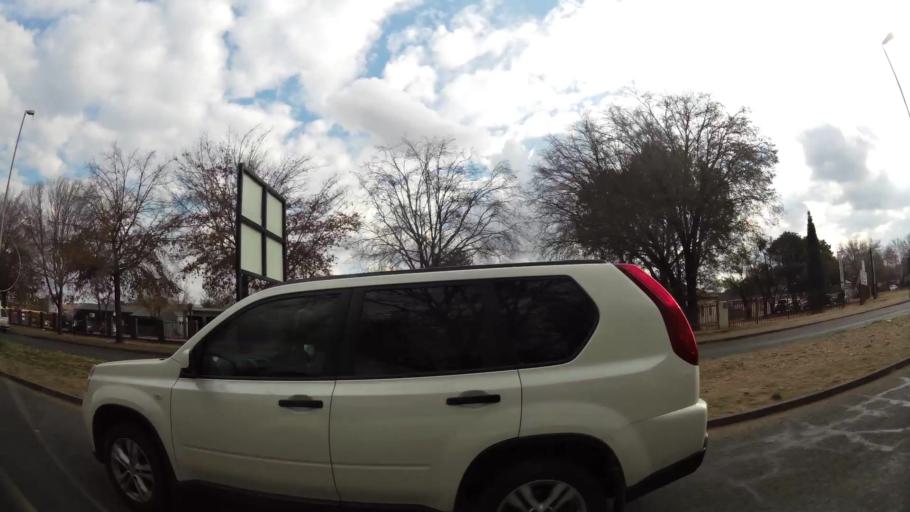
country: ZA
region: Orange Free State
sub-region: Fezile Dabi District Municipality
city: Sasolburg
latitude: -26.8108
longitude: 27.8281
